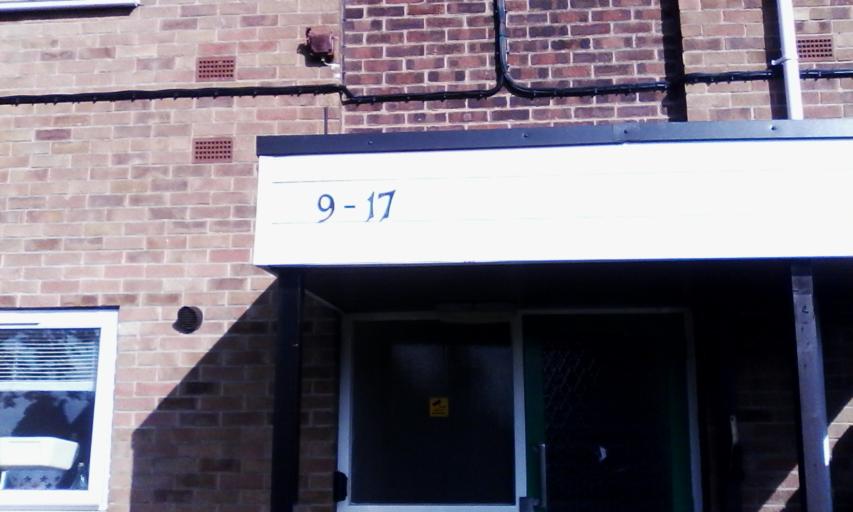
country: GB
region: England
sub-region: Nottinghamshire
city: Arnold
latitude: 52.9830
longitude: -1.1136
